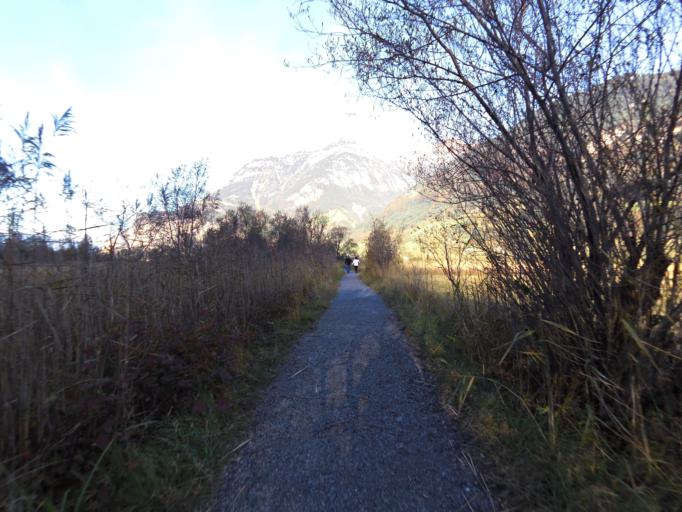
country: CH
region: Uri
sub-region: Uri
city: Flueelen
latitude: 46.8971
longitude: 8.6152
